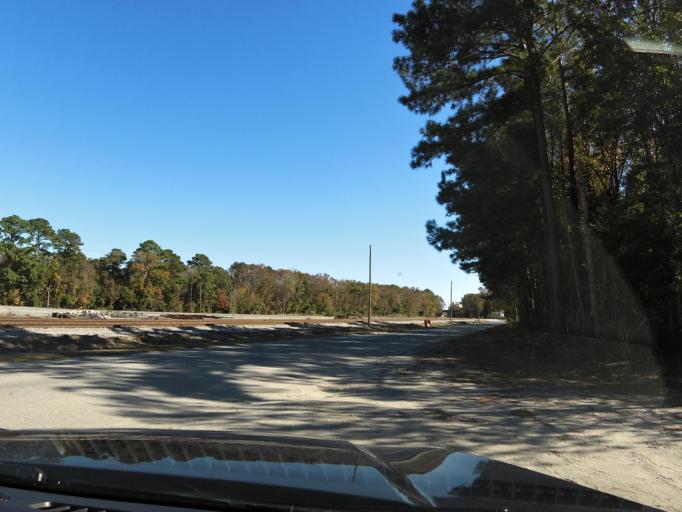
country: US
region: Georgia
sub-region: Chatham County
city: Garden City
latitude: 32.0929
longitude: -81.1609
